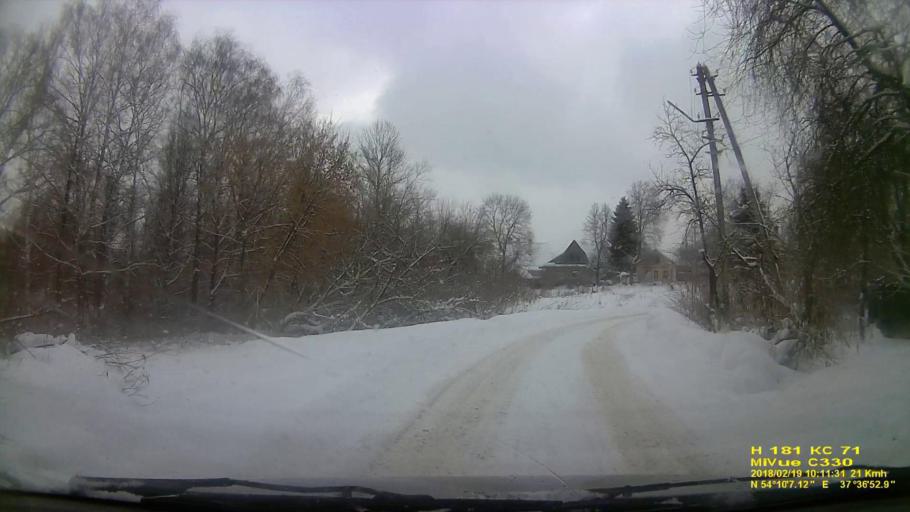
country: RU
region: Tula
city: Tula
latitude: 54.1692
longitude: 37.6161
